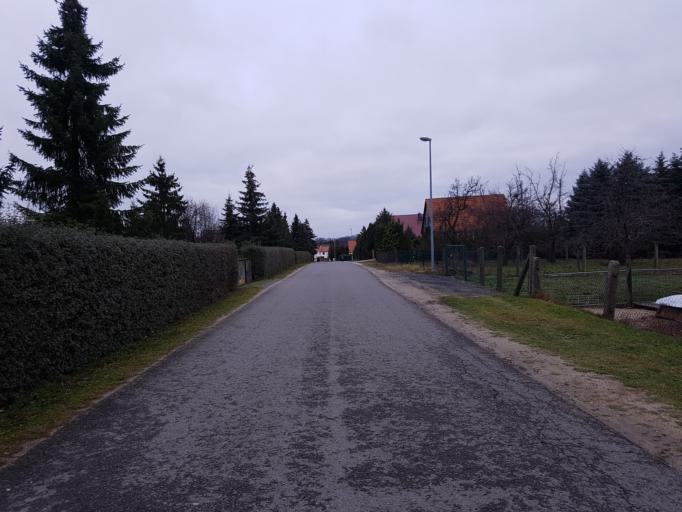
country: DE
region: Brandenburg
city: Groden
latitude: 51.4031
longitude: 13.5780
